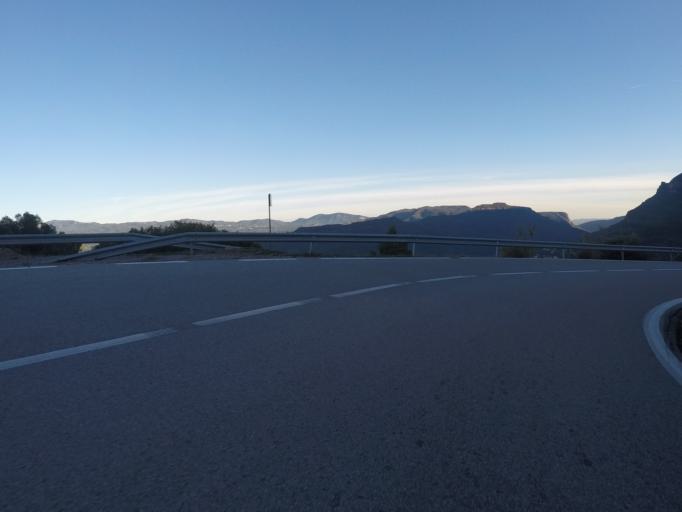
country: ES
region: Catalonia
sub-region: Provincia de Barcelona
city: Monistrol de Montserrat
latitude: 41.6160
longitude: 1.8379
